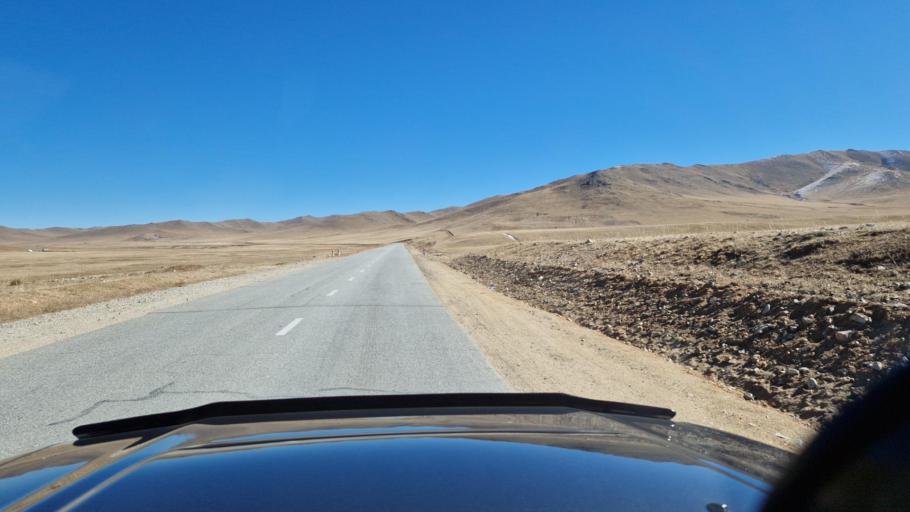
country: MN
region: Central Aimak
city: Bayandelger
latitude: 47.6938
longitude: 108.5271
